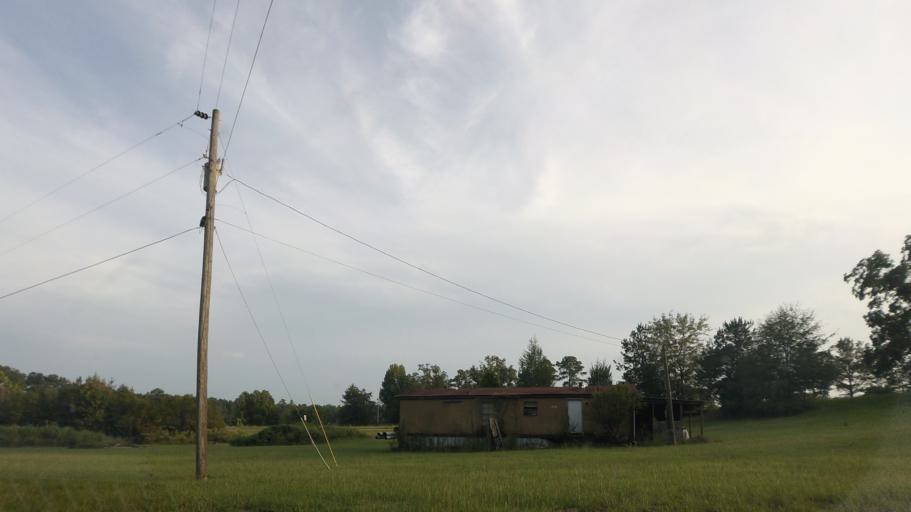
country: US
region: Georgia
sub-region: Wilkinson County
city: Gordon
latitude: 32.8489
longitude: -83.4238
